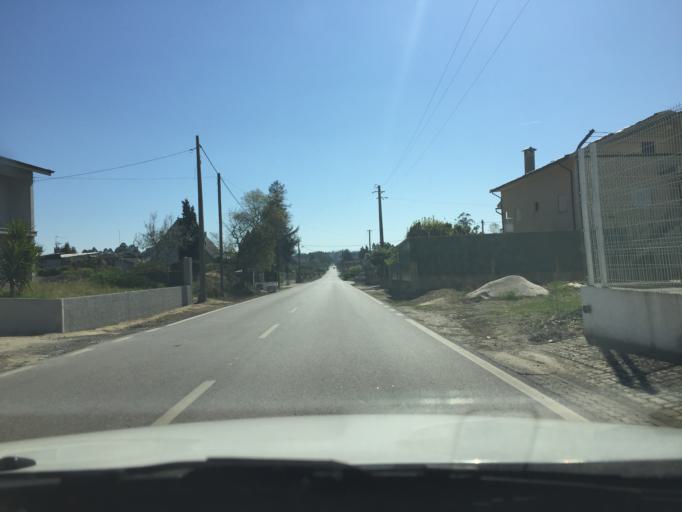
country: PT
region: Coimbra
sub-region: Cantanhede
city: Cantanhede
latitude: 40.4222
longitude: -8.5785
